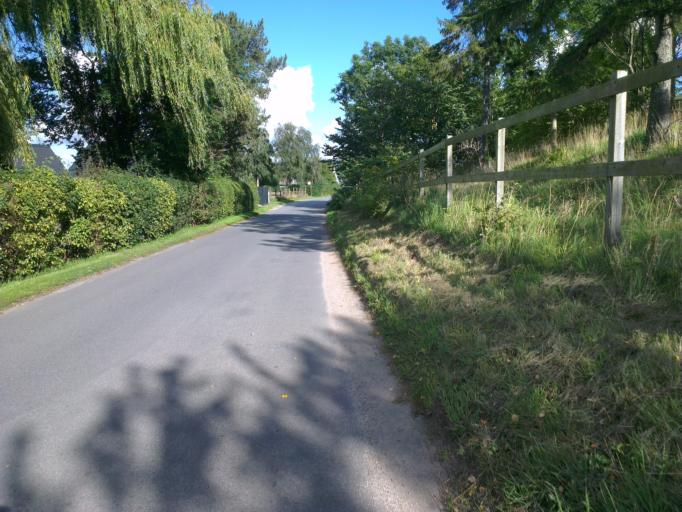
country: DK
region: Capital Region
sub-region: Frederikssund Kommune
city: Frederikssund
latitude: 55.7886
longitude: 12.0403
